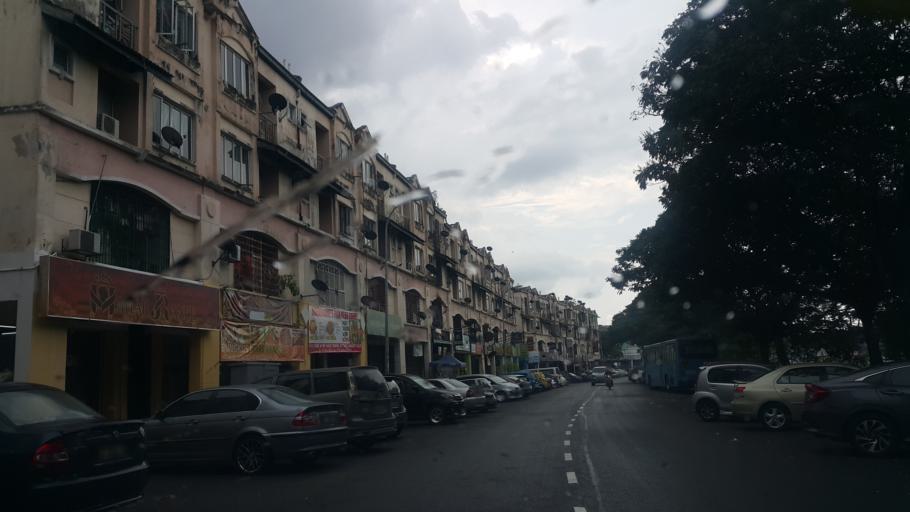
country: MY
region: Selangor
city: Klang
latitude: 3.0084
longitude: 101.4388
